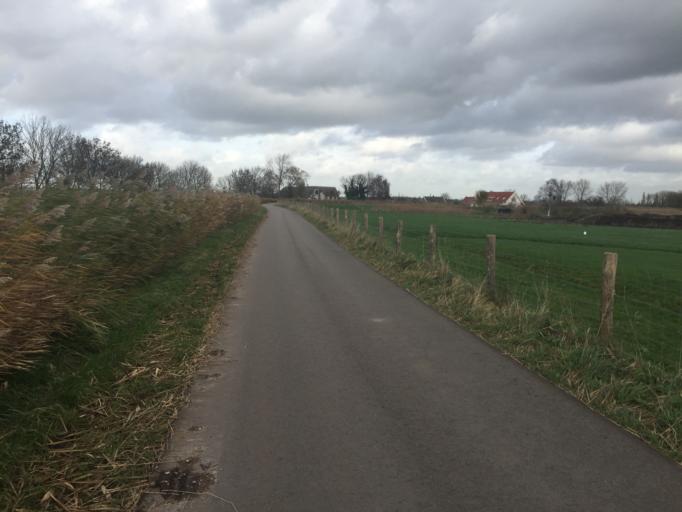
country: NL
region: North Holland
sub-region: Gemeente Ouder-Amstel
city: Ouderkerk aan de Amstel
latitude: 52.2601
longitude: 4.9185
